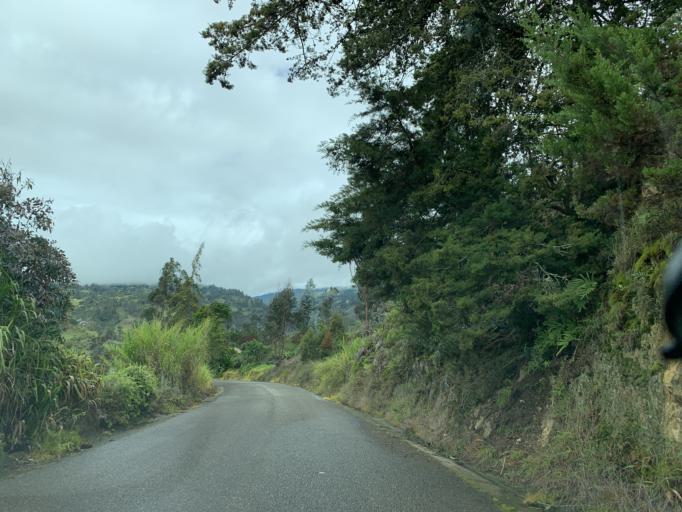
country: CO
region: Boyaca
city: Tibana
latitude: 5.3117
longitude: -73.4158
